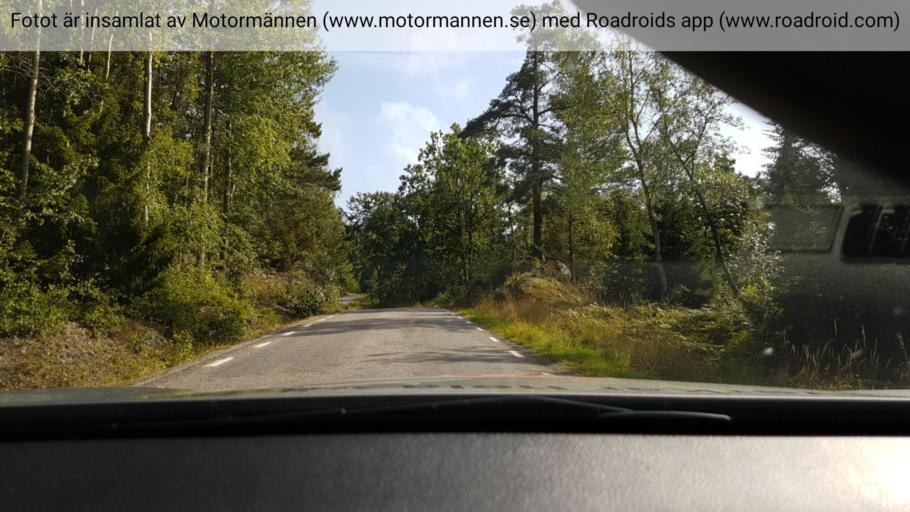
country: SE
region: Stockholm
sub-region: Nynashamns Kommun
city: Osmo
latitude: 58.8814
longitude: 17.7898
